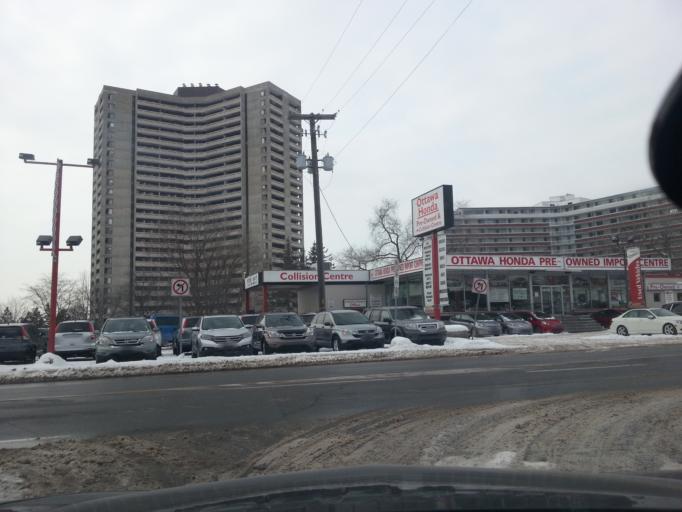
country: CA
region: Ontario
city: Bells Corners
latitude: 45.3727
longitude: -75.7794
